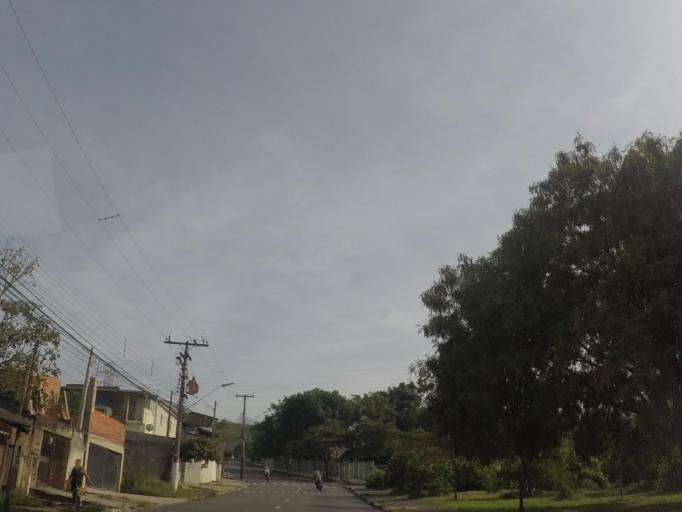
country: BR
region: Sao Paulo
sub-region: Hortolandia
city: Hortolandia
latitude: -22.8646
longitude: -47.2000
